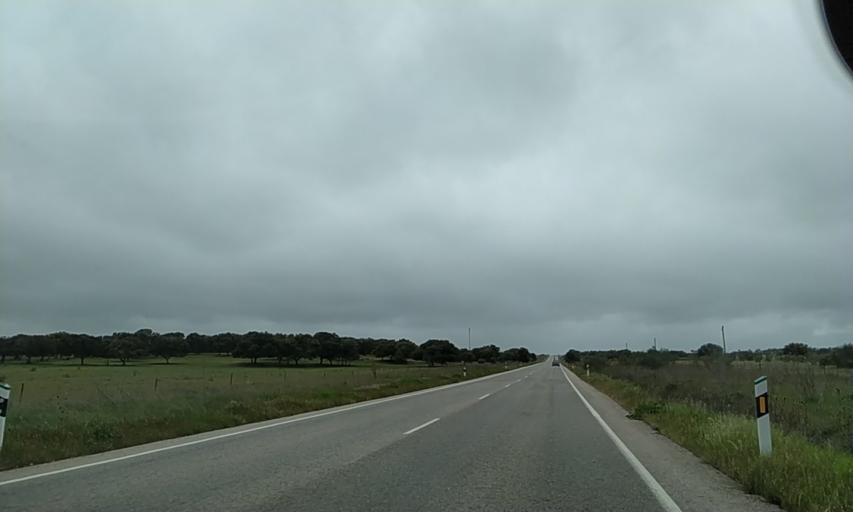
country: ES
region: Extremadura
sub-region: Provincia de Caceres
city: Malpartida de Caceres
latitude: 39.3712
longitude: -6.4554
